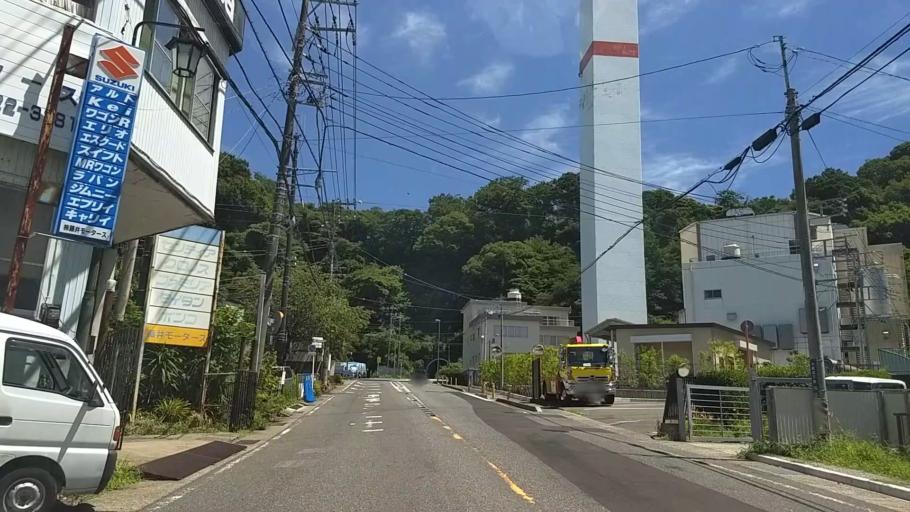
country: JP
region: Kanagawa
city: Kamakura
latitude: 35.3089
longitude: 139.5607
